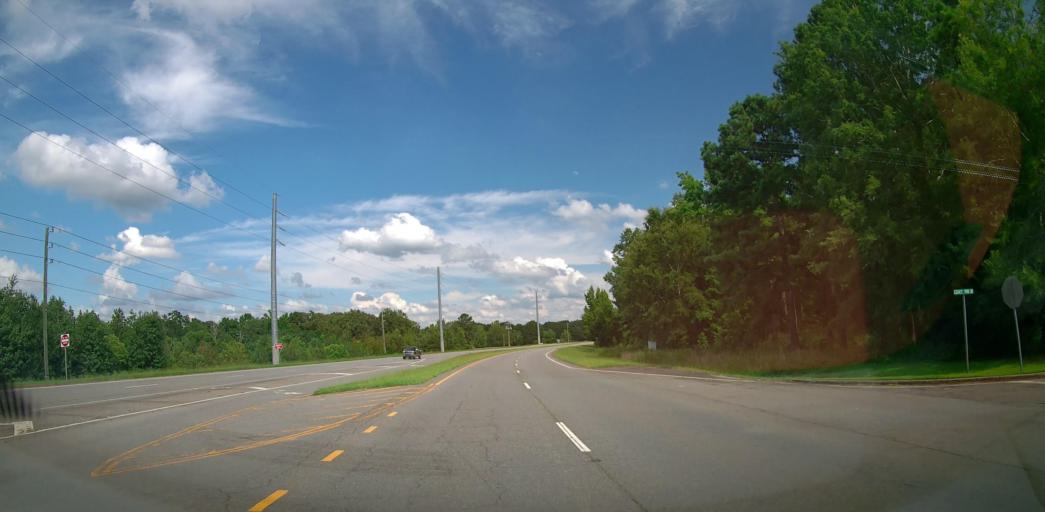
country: US
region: Georgia
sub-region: Houston County
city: Perry
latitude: 32.4863
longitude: -83.7177
